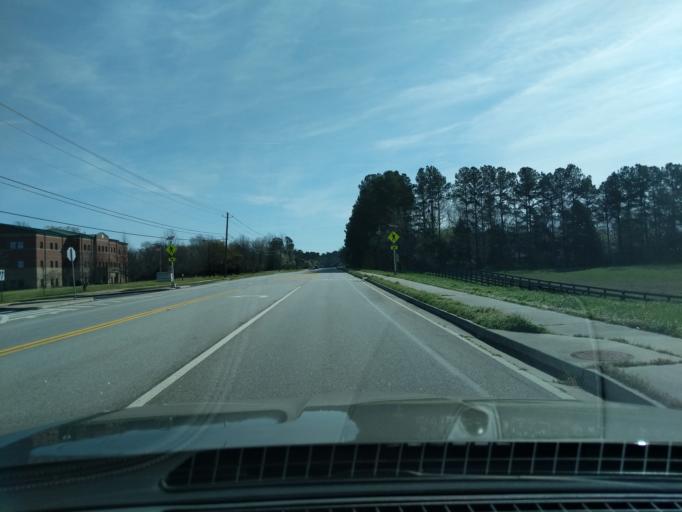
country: US
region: Georgia
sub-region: Columbia County
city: Evans
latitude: 33.5303
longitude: -82.1601
